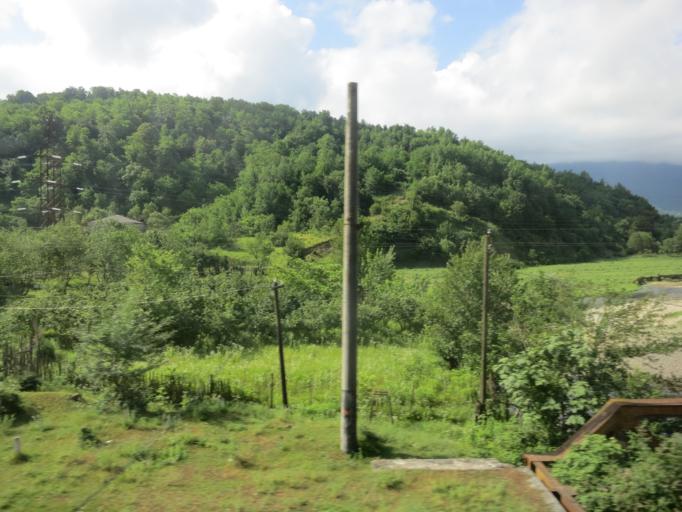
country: GE
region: Imereti
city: Samtredia
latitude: 42.0978
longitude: 42.2546
